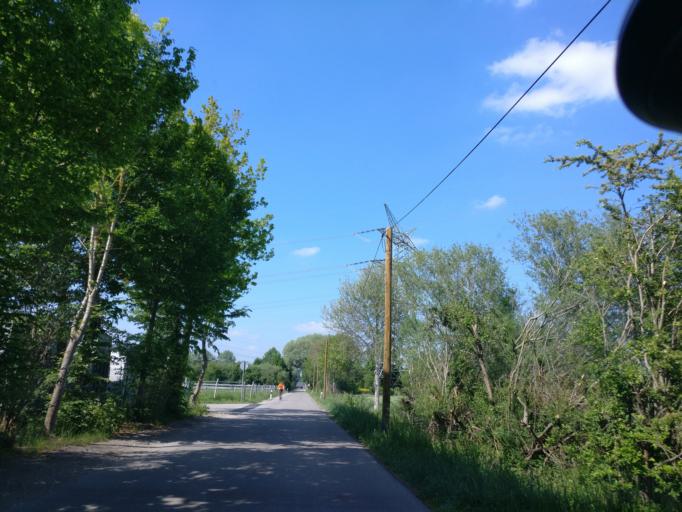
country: DE
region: Bavaria
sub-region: Upper Bavaria
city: Karlsfeld
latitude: 48.2136
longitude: 11.4333
